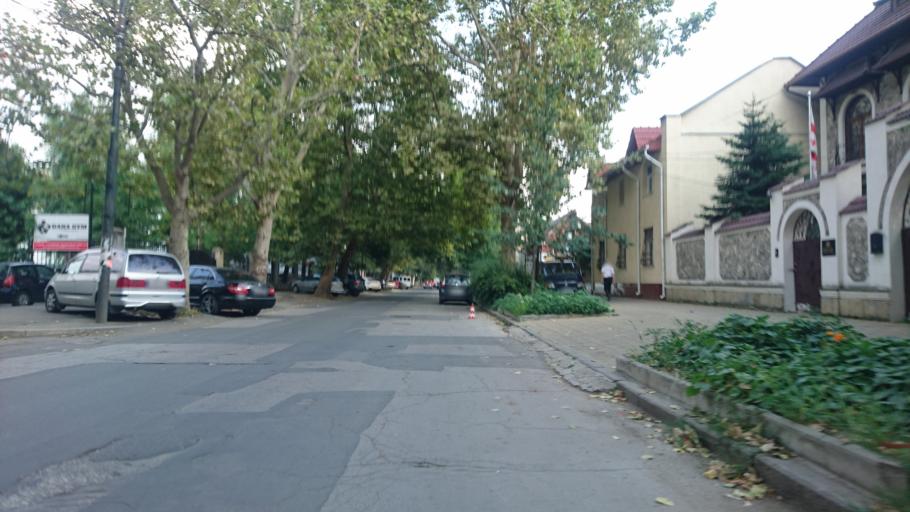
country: MD
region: Chisinau
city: Chisinau
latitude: 47.0161
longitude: 28.8392
